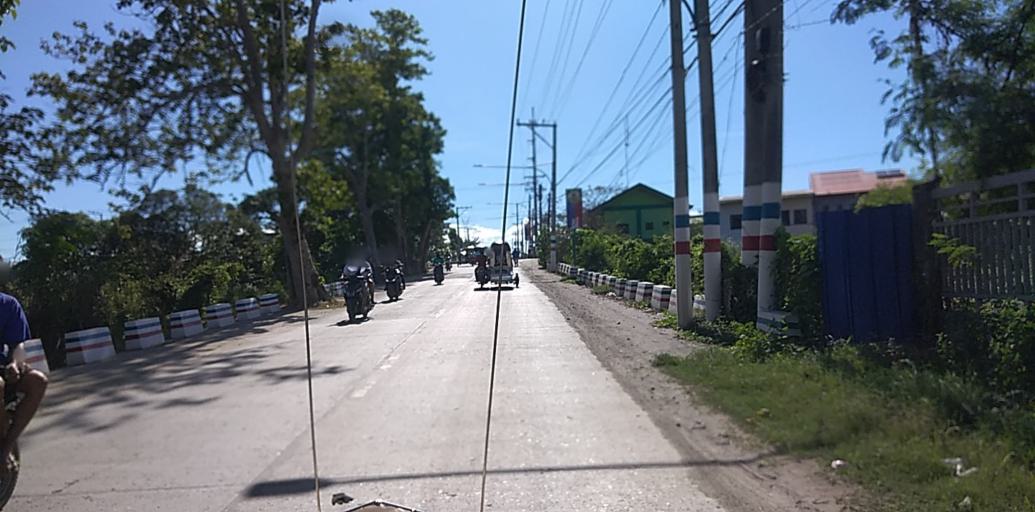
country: PH
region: Central Luzon
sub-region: Province of Pampanga
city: San Luis
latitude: 15.0456
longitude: 120.7871
